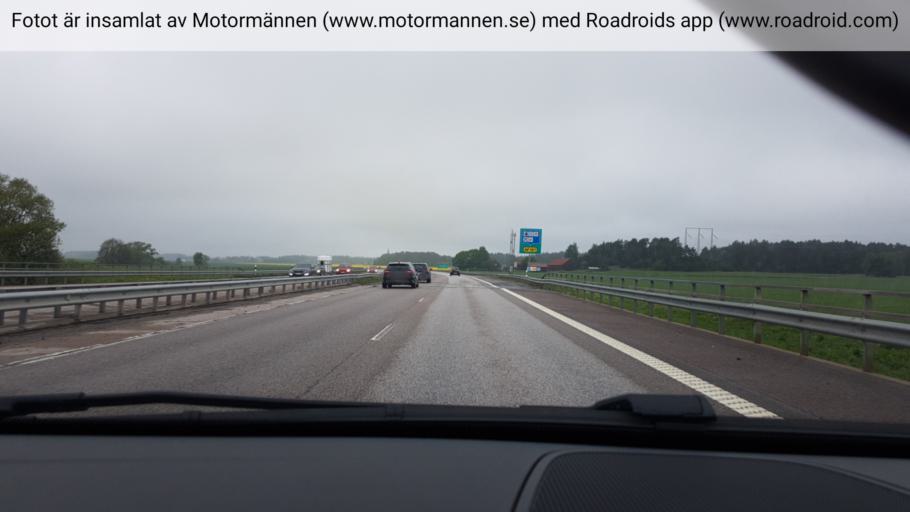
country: SE
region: Uppsala
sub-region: Uppsala Kommun
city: Saevja
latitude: 59.8149
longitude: 17.7550
